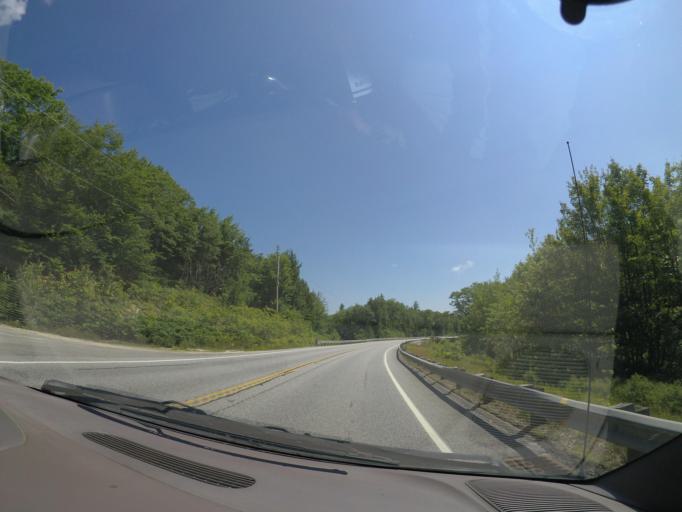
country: US
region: New Hampshire
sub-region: Hillsborough County
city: Antrim
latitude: 43.0738
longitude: -72.0467
